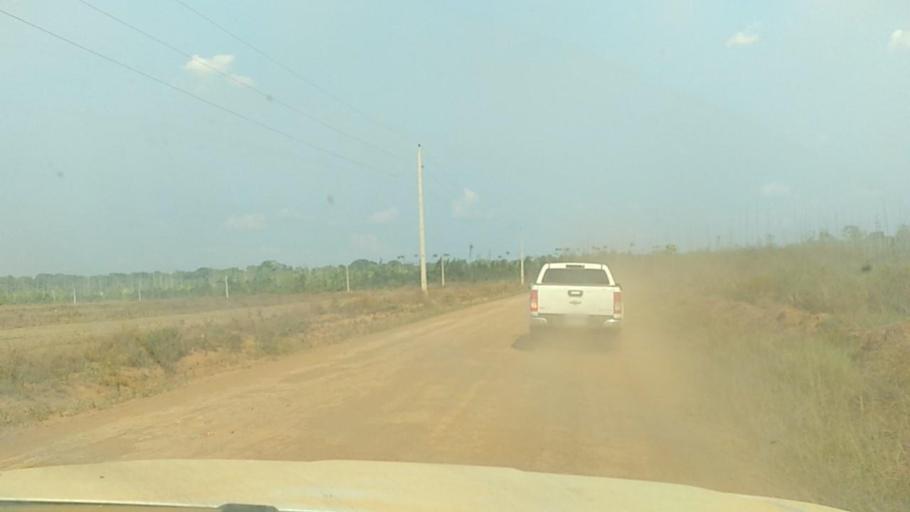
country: BR
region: Rondonia
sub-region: Porto Velho
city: Porto Velho
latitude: -8.6729
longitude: -64.0203
